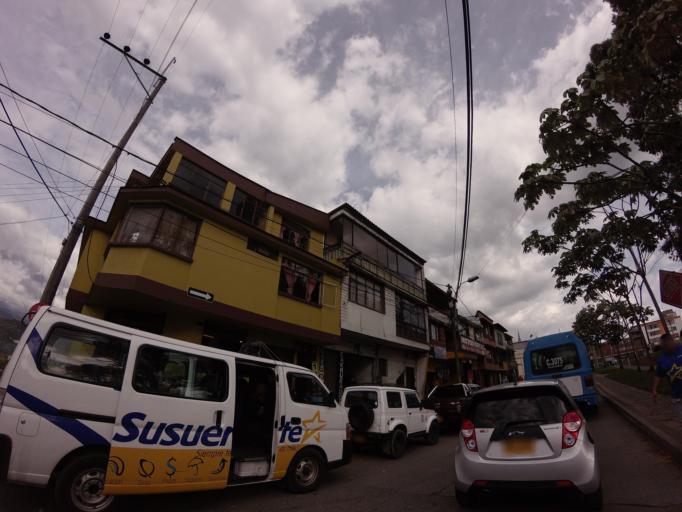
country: CO
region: Caldas
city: Manizales
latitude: 5.0742
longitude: -75.5185
